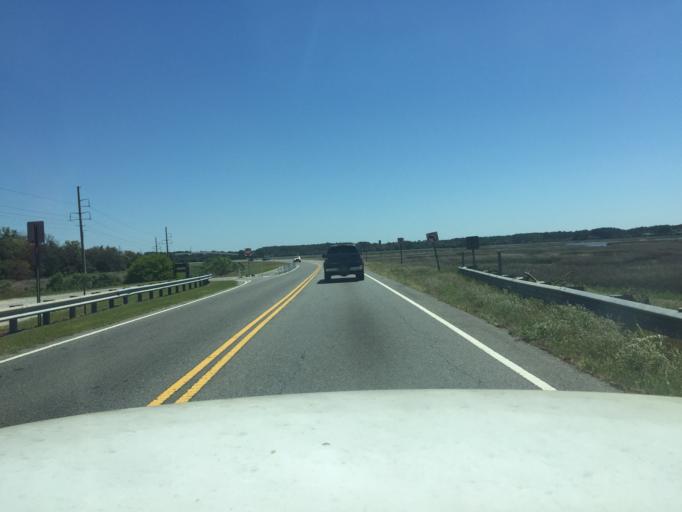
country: US
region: Georgia
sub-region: Chatham County
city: Isle of Hope
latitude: 31.9507
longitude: -81.0815
